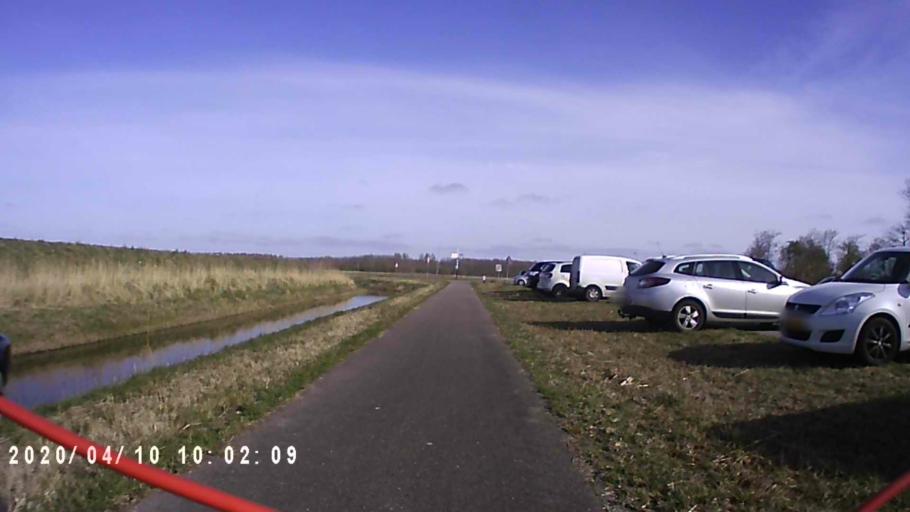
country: NL
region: Groningen
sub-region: Gemeente De Marne
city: Ulrum
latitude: 53.3637
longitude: 6.2605
